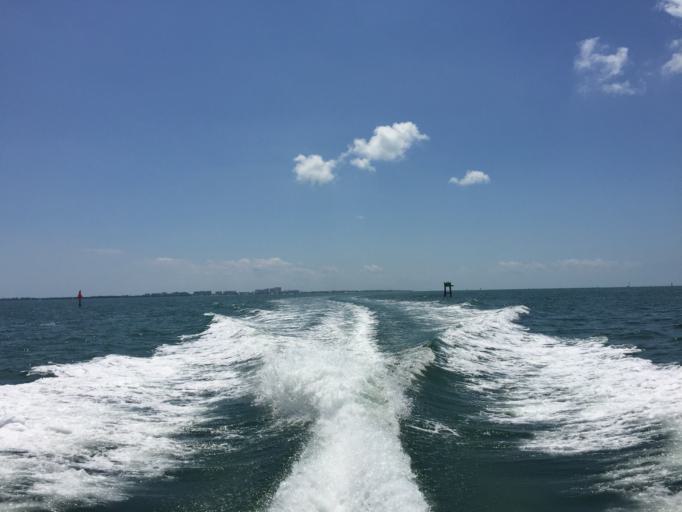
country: US
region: Florida
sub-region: Miami-Dade County
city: Coconut Grove
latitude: 25.7213
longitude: -80.2172
